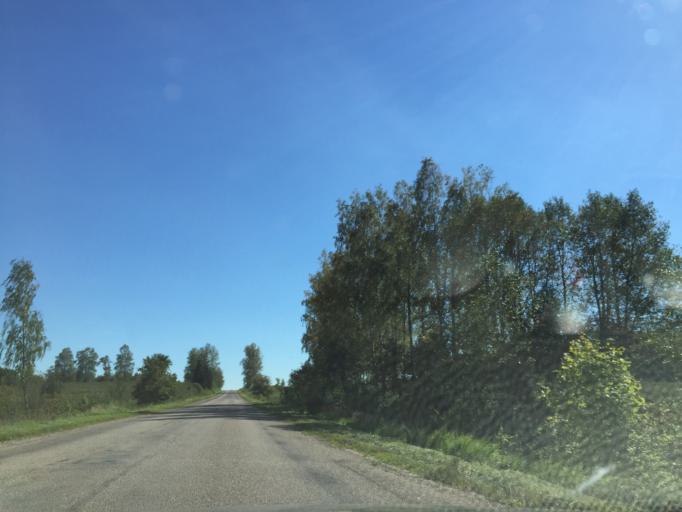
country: LV
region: Akniste
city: Akniste
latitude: 56.0337
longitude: 25.9115
